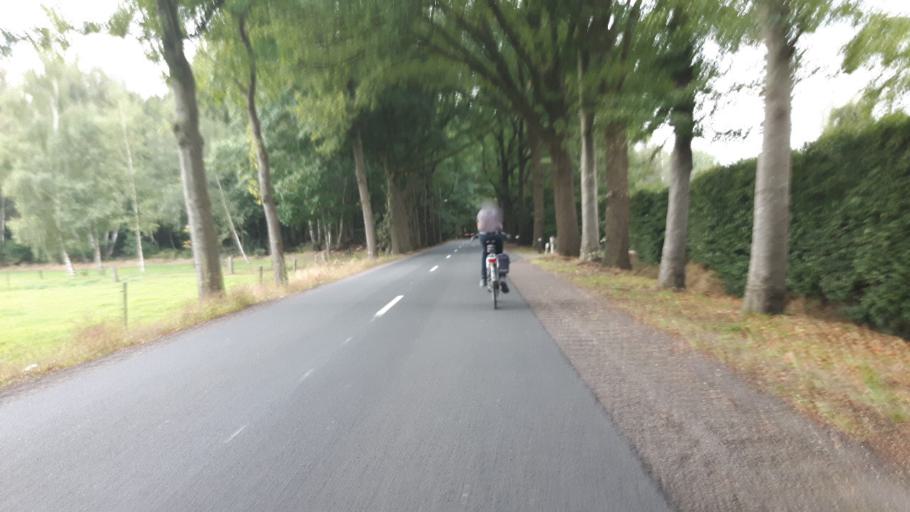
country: NL
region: Gelderland
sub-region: Gemeente Barneveld
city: Zwartebroek
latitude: 52.2070
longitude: 5.5324
